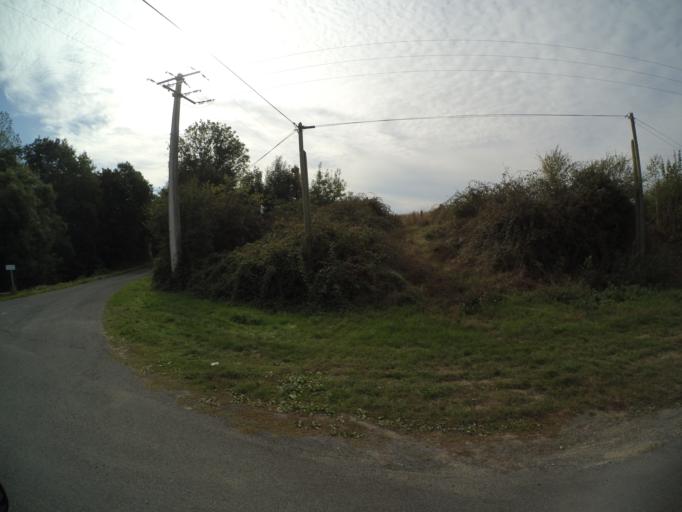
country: FR
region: Pays de la Loire
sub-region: Departement de Maine-et-Loire
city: Villedieu-la-Blouere
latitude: 47.1546
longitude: -1.0459
